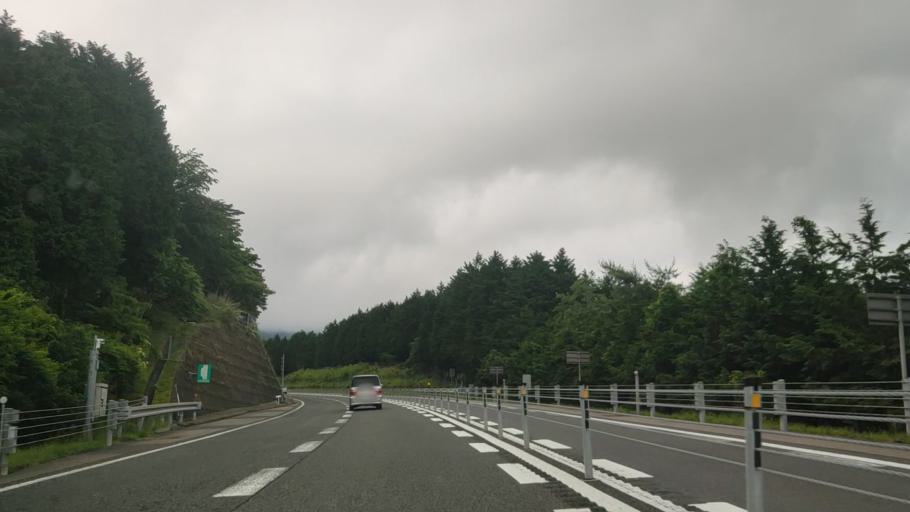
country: JP
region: Shizuoka
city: Gotemba
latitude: 35.3700
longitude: 138.8495
